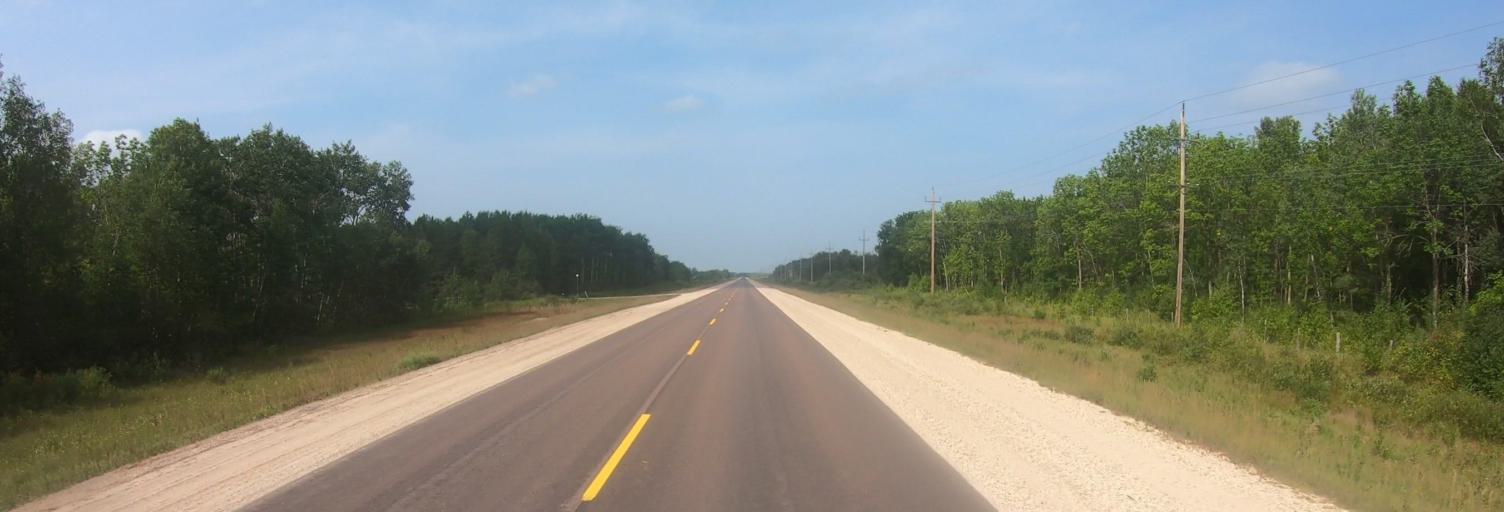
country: CA
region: Manitoba
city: La Broquerie
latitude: 49.2670
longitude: -96.4472
